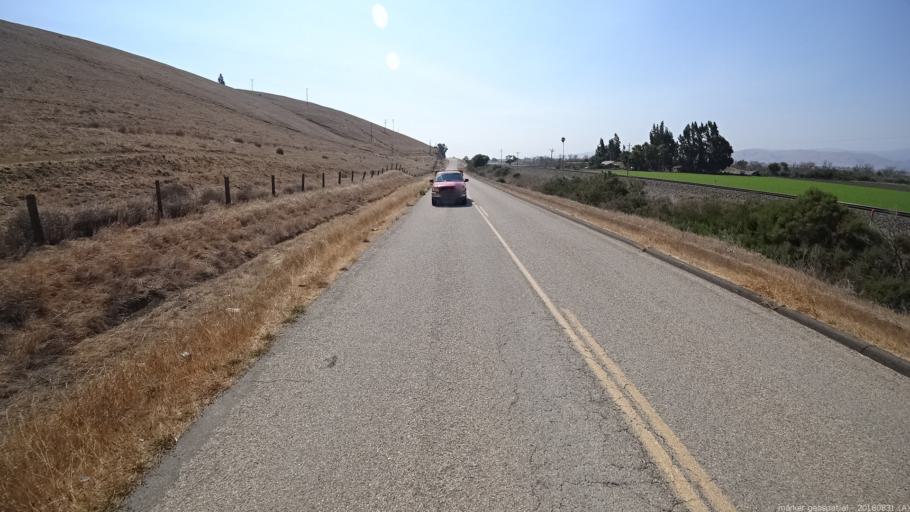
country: US
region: California
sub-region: Monterey County
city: Greenfield
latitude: 36.3663
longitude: -121.2347
